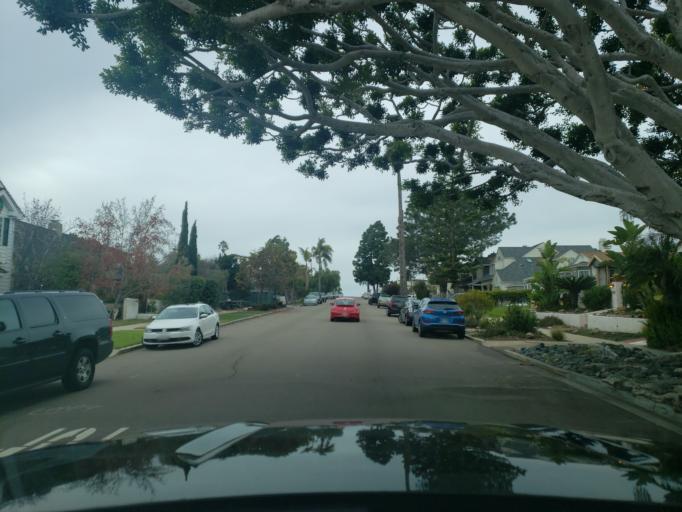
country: US
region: California
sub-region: San Diego County
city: Coronado
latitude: 32.7344
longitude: -117.2434
